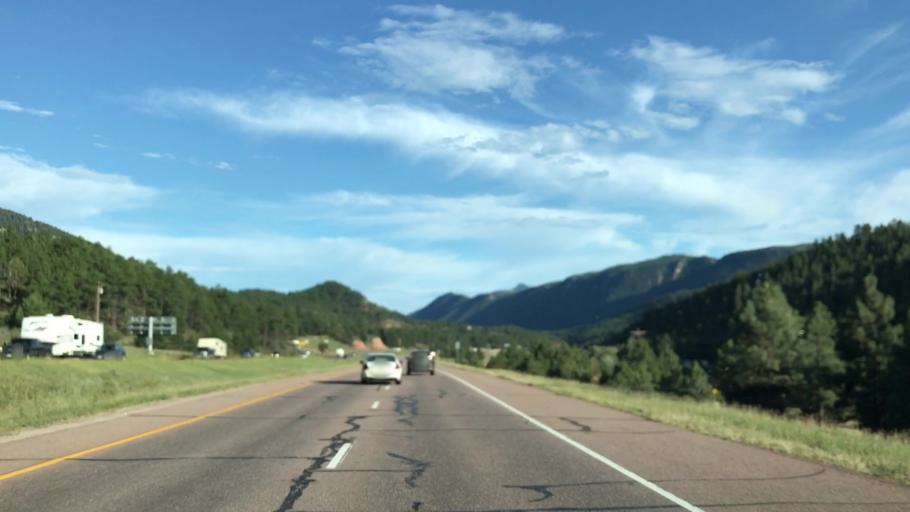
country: US
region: Colorado
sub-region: Teller County
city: Woodland Park
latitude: 38.9663
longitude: -105.0332
